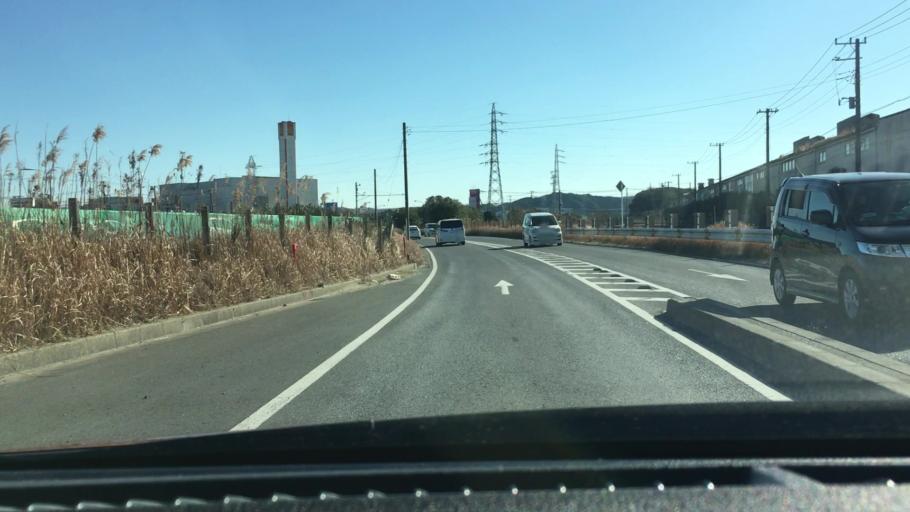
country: JP
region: Chiba
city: Kisarazu
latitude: 35.3723
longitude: 139.9080
